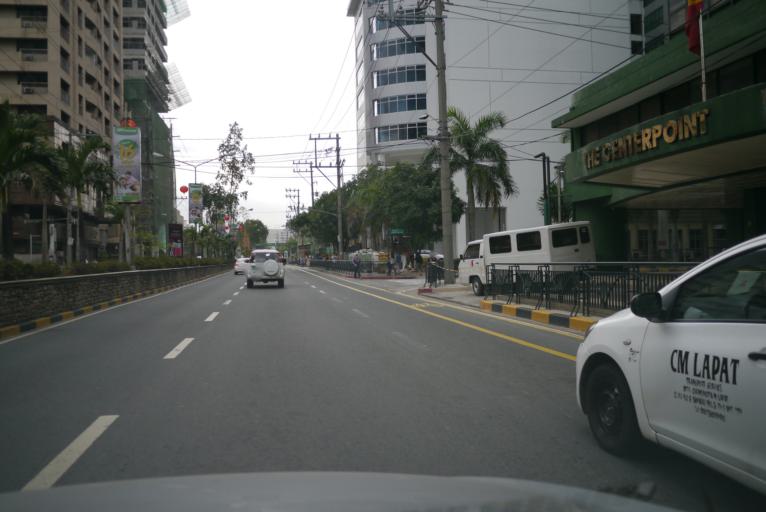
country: PH
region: Metro Manila
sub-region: Pasig
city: Pasig City
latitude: 14.5844
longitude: 121.0627
